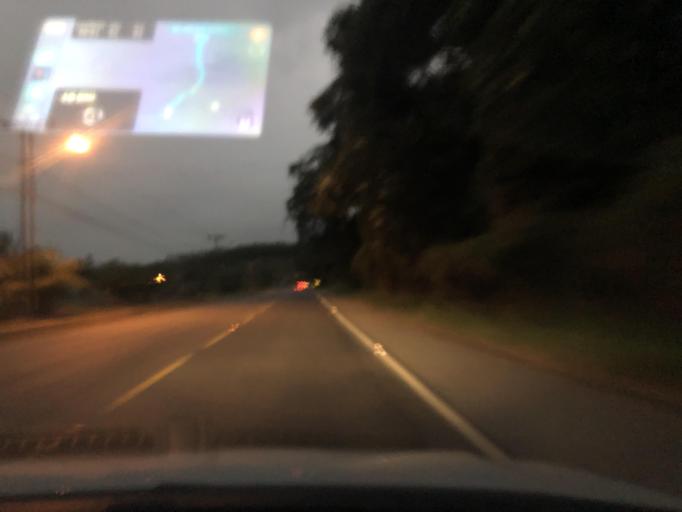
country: BR
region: Santa Catarina
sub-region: Guaramirim
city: Guaramirim
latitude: -26.5964
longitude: -48.9981
